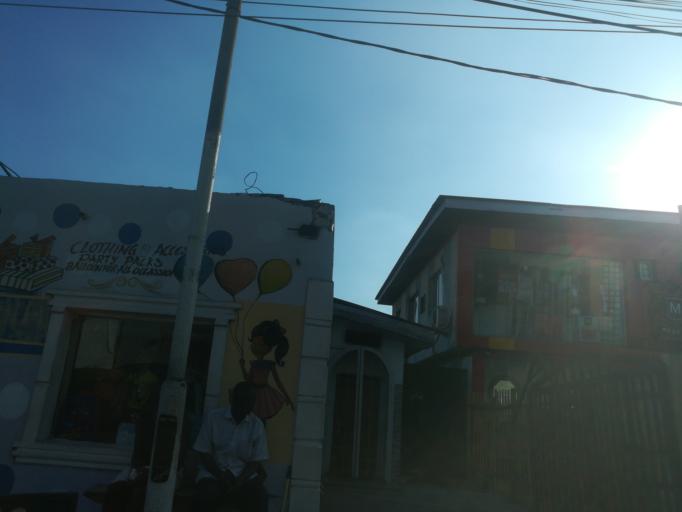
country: NG
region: Lagos
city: Ojota
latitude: 6.5849
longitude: 3.3650
